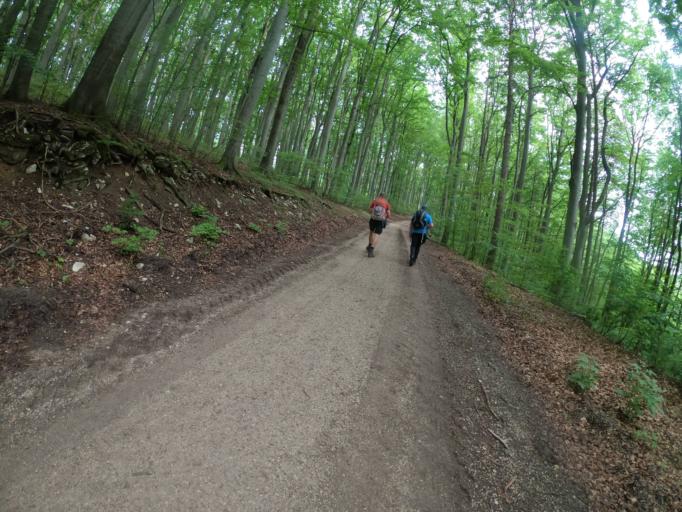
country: DE
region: Bavaria
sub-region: Upper Franconia
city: Litzendorf
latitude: 49.9258
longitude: 11.0389
